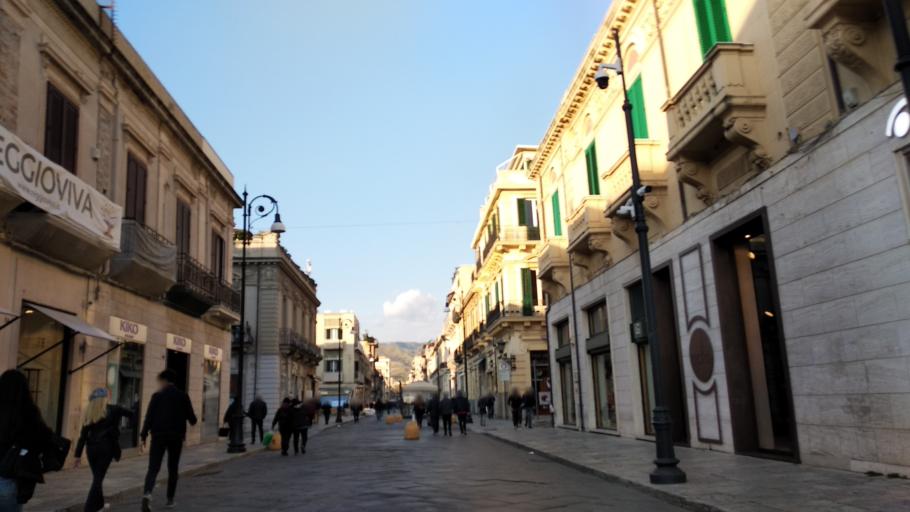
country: IT
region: Calabria
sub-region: Provincia di Reggio Calabria
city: Reggio Calabria
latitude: 38.1092
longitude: 15.6451
